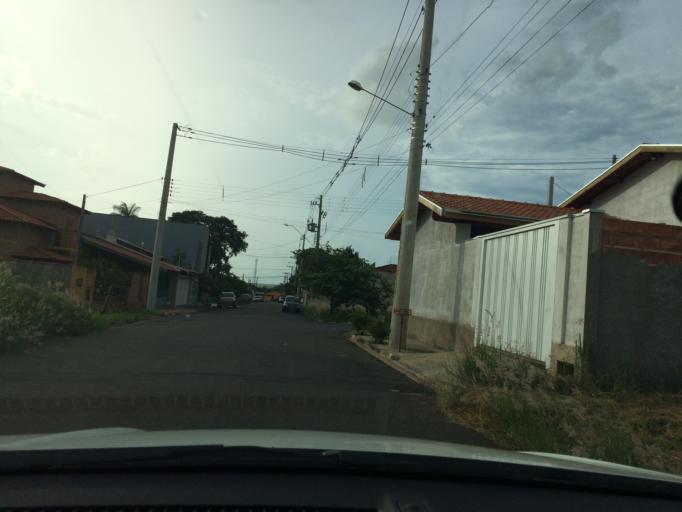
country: BR
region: Sao Paulo
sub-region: Casa Branca
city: Casa Branca
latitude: -21.7807
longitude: -47.0847
